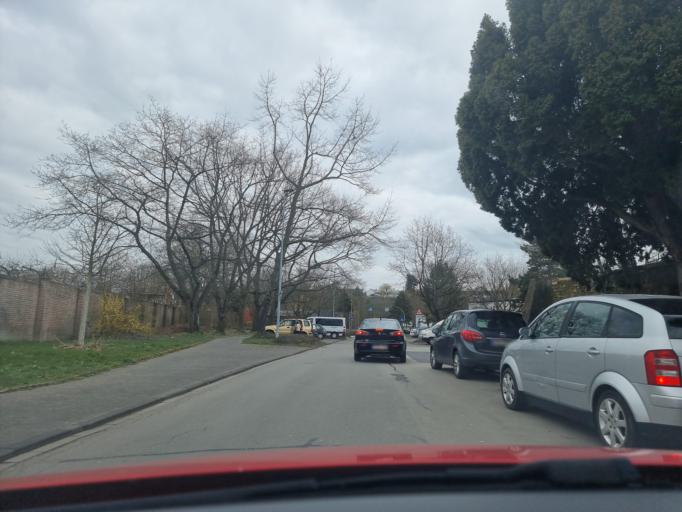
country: DE
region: Rheinland-Pfalz
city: Trier
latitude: 49.7361
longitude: 6.6300
